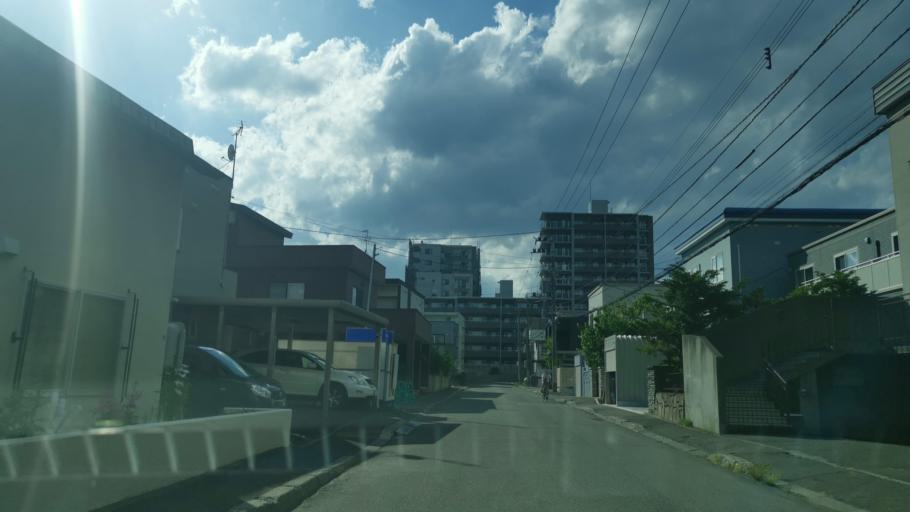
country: JP
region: Hokkaido
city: Sapporo
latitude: 43.0678
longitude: 141.2977
